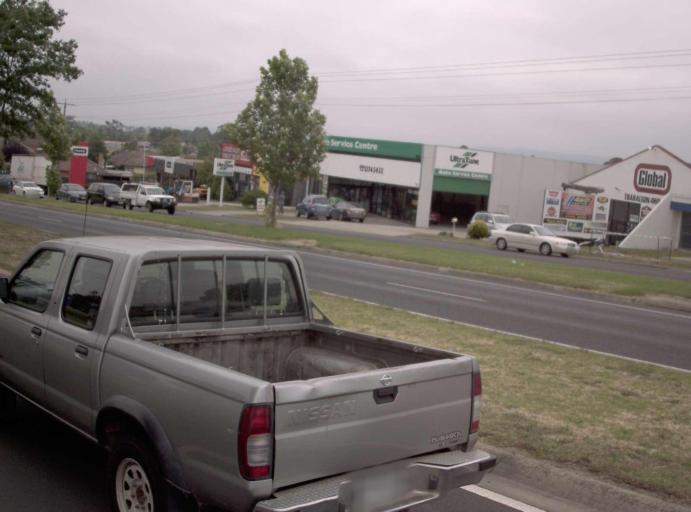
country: AU
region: Victoria
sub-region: Latrobe
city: Traralgon
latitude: -38.1918
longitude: 146.5556
